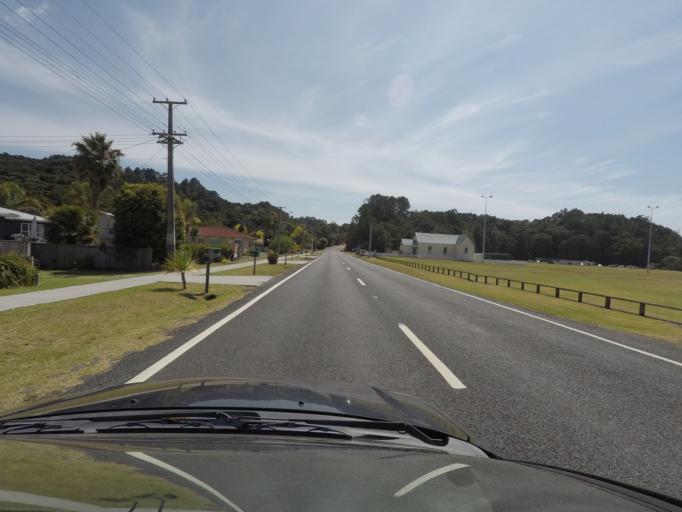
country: NZ
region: Auckland
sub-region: Auckland
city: Warkworth
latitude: -36.3140
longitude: 174.7660
